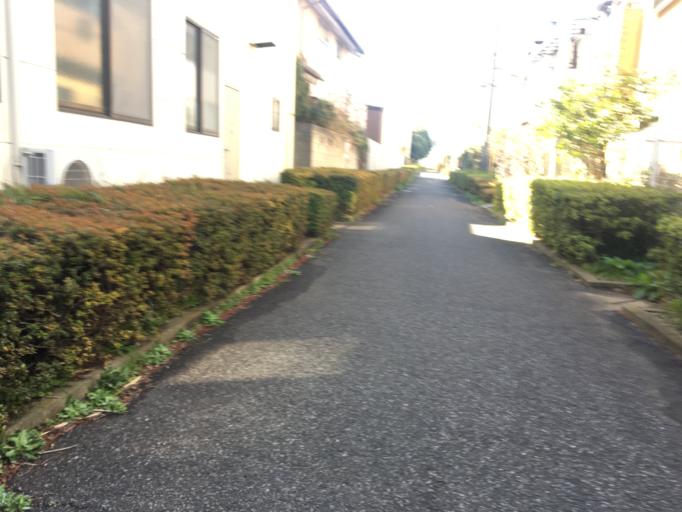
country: JP
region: Saitama
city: Shiki
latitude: 35.8042
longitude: 139.5658
